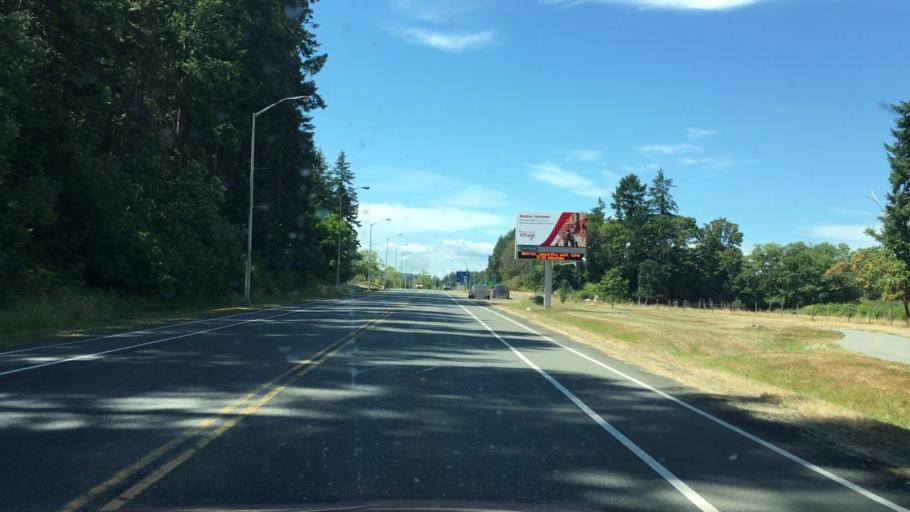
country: CA
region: British Columbia
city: North Saanich
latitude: 48.6358
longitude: -123.4253
